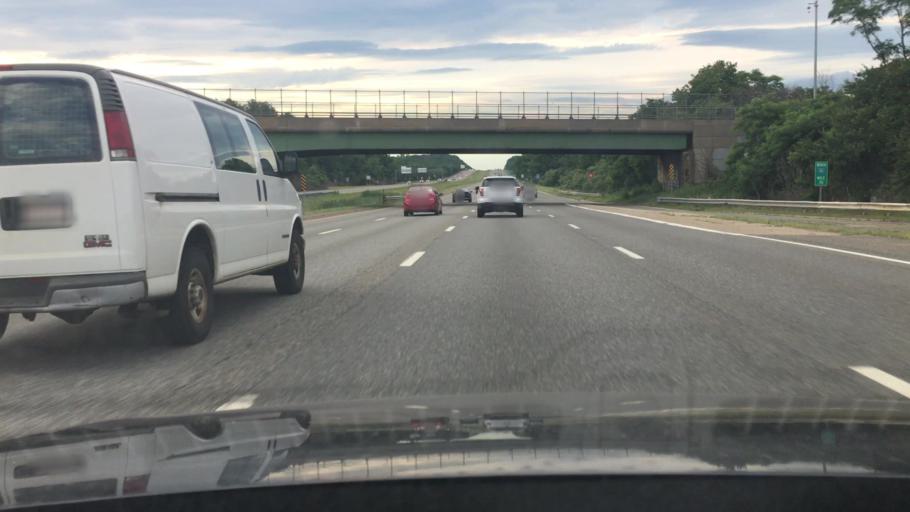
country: US
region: Massachusetts
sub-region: Essex County
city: Danvers
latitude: 42.5954
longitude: -70.9630
